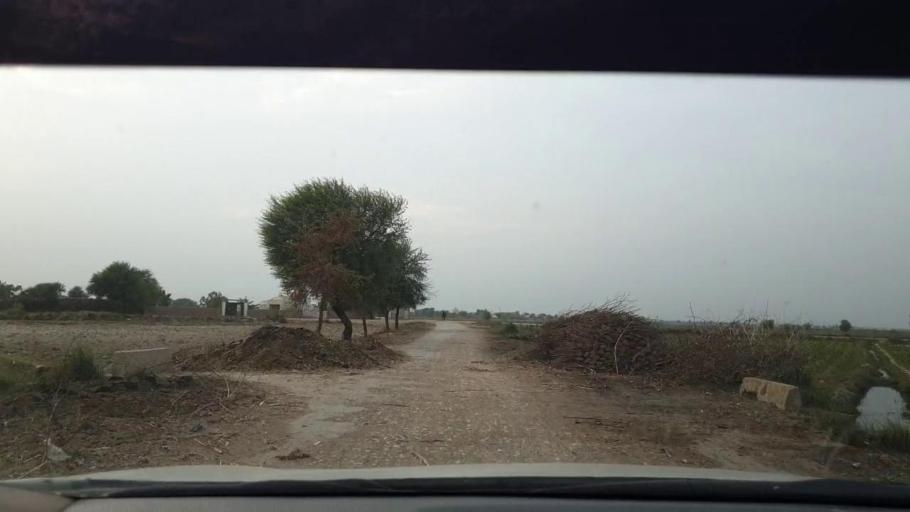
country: PK
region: Sindh
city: Jhol
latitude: 25.9105
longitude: 68.7716
